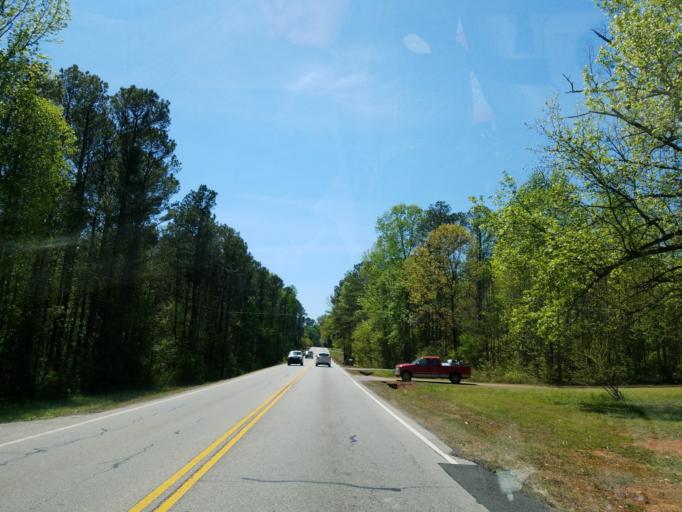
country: US
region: Georgia
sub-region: Paulding County
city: Hiram
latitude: 33.8678
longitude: -84.7869
